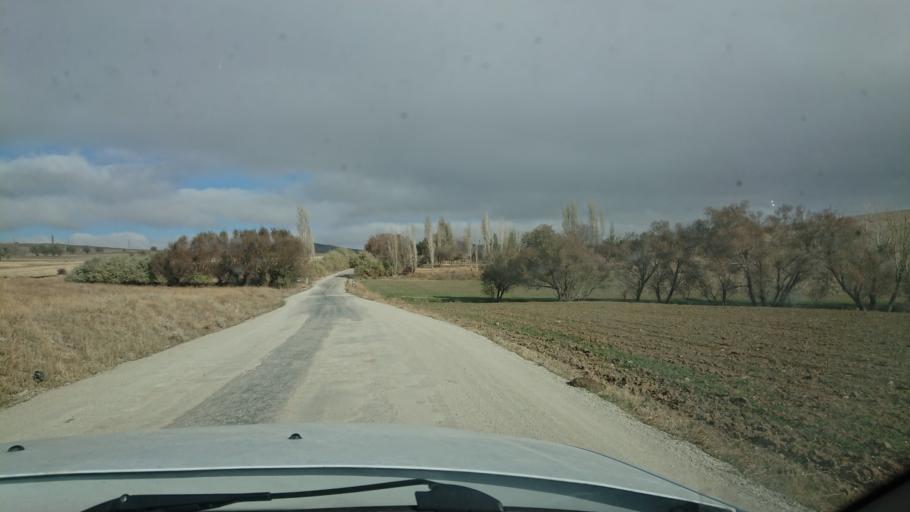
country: TR
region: Aksaray
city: Ortakoy
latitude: 38.7655
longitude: 34.0143
